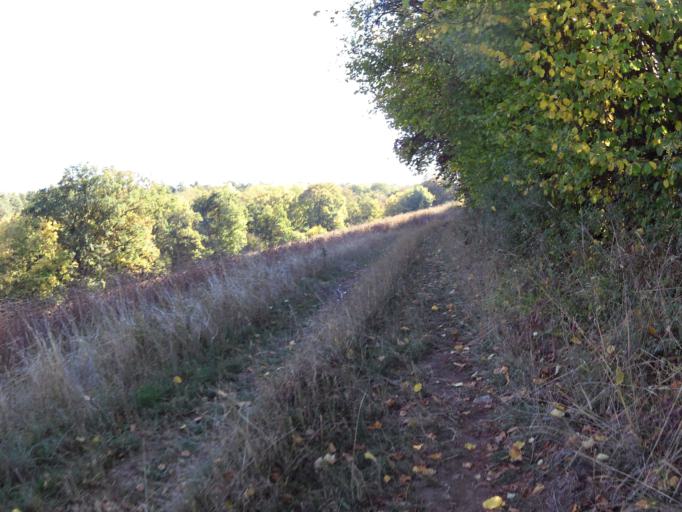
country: DE
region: Bavaria
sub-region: Regierungsbezirk Unterfranken
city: Eibelstadt
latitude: 49.7203
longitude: 9.9840
